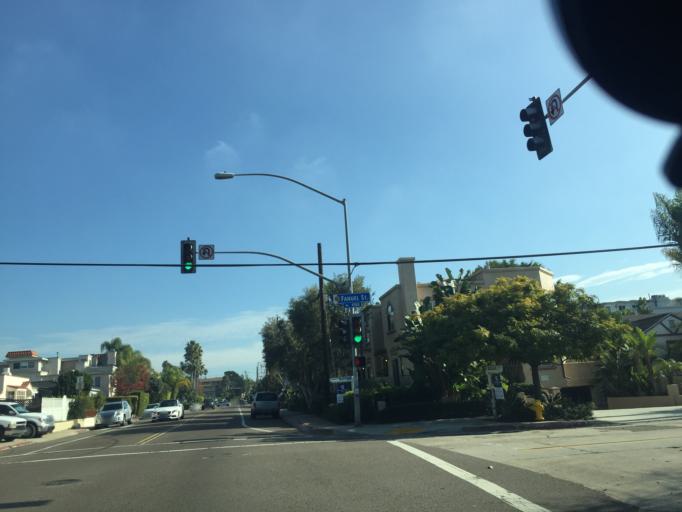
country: US
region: California
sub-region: San Diego County
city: La Jolla
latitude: 32.7929
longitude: -117.2447
